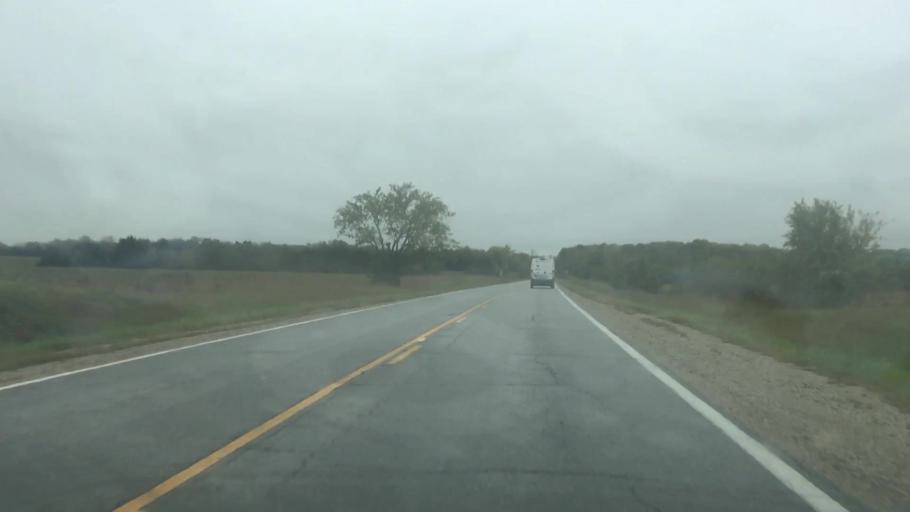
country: US
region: Kansas
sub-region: Anderson County
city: Garnett
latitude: 38.2389
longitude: -95.2479
